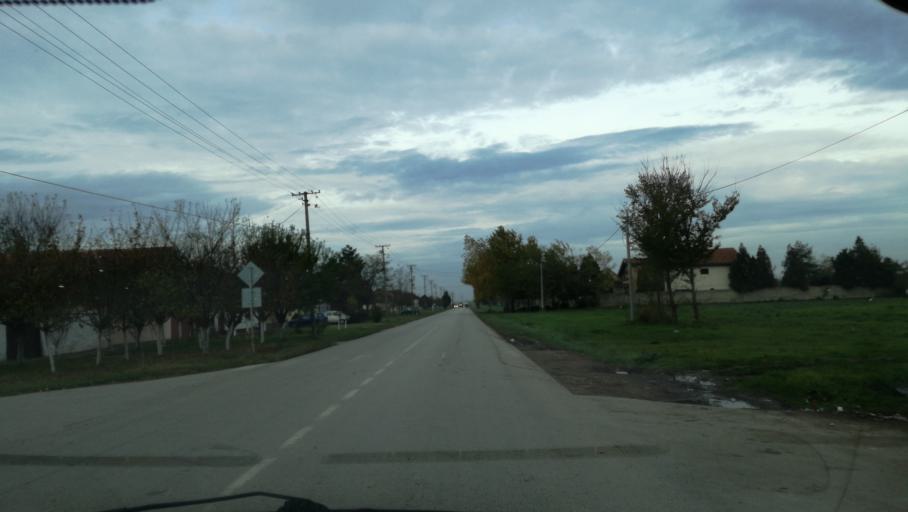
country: RS
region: Autonomna Pokrajina Vojvodina
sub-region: Severnobanatski Okrug
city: Kikinda
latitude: 45.8430
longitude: 20.4610
